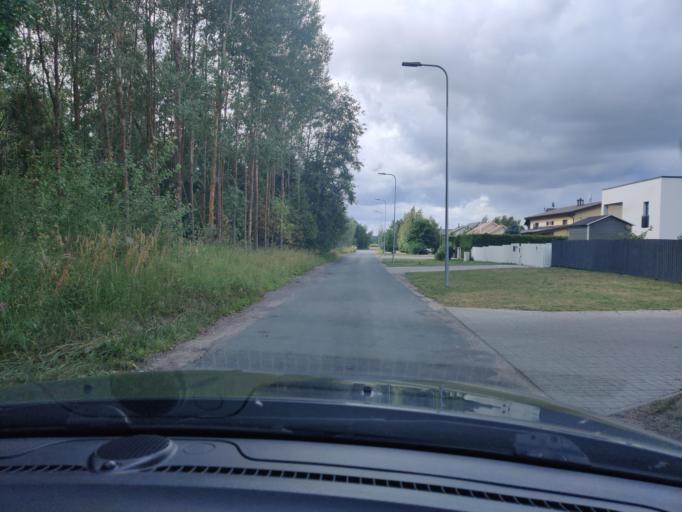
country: EE
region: Harju
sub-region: Saue vald
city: Laagri
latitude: 59.4257
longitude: 24.6276
